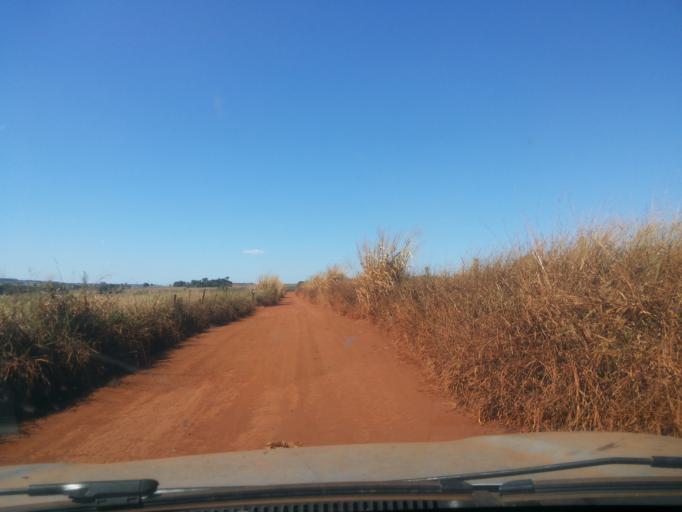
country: BR
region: Minas Gerais
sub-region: Centralina
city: Centralina
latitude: -18.7394
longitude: -49.1995
